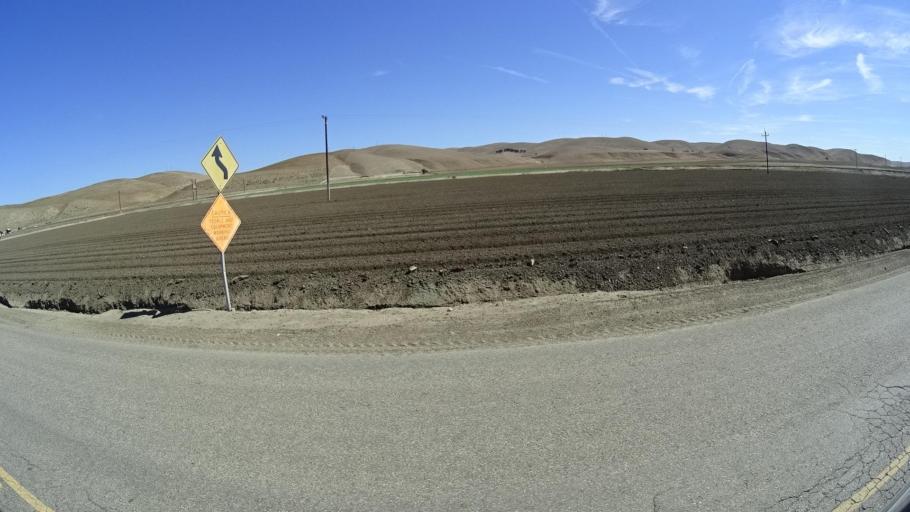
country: US
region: California
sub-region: San Luis Obispo County
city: Lake Nacimiento
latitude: 36.0070
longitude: -120.8865
